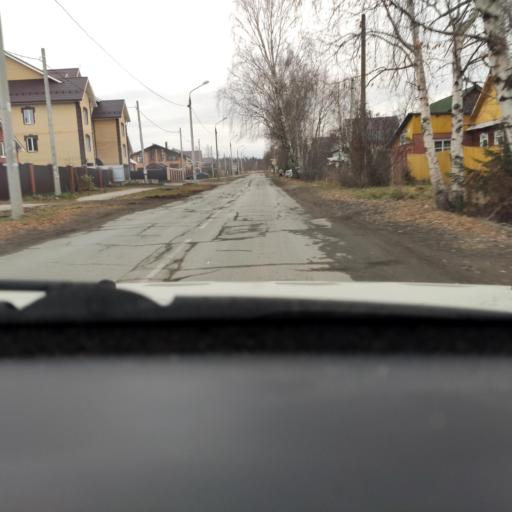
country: RU
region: Perm
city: Polazna
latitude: 58.1273
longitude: 56.4010
